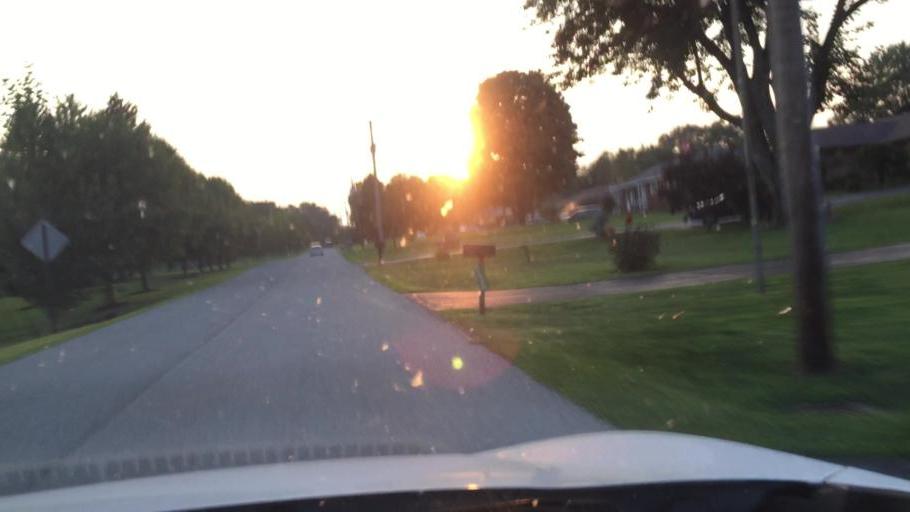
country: US
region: Ohio
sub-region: Clark County
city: Lisbon
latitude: 39.9444
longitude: -83.5897
